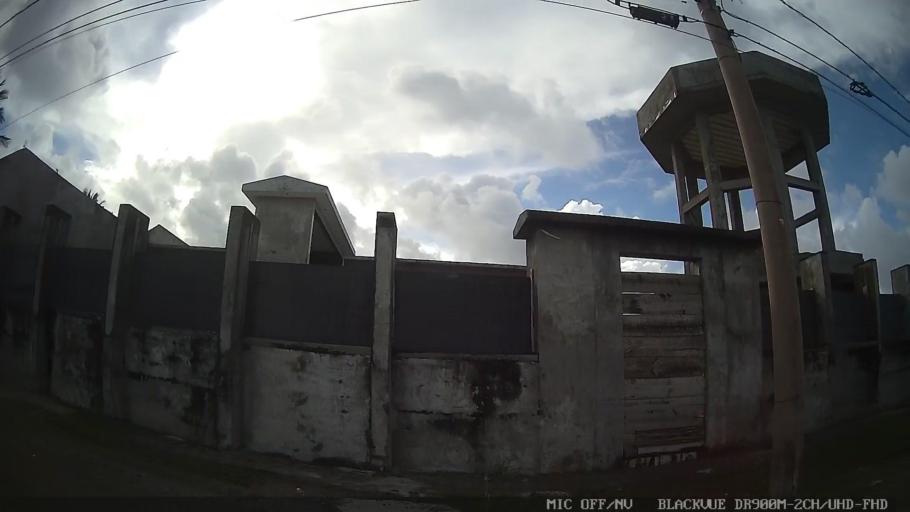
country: BR
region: Sao Paulo
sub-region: Itanhaem
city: Itanhaem
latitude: -24.2064
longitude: -46.8275
